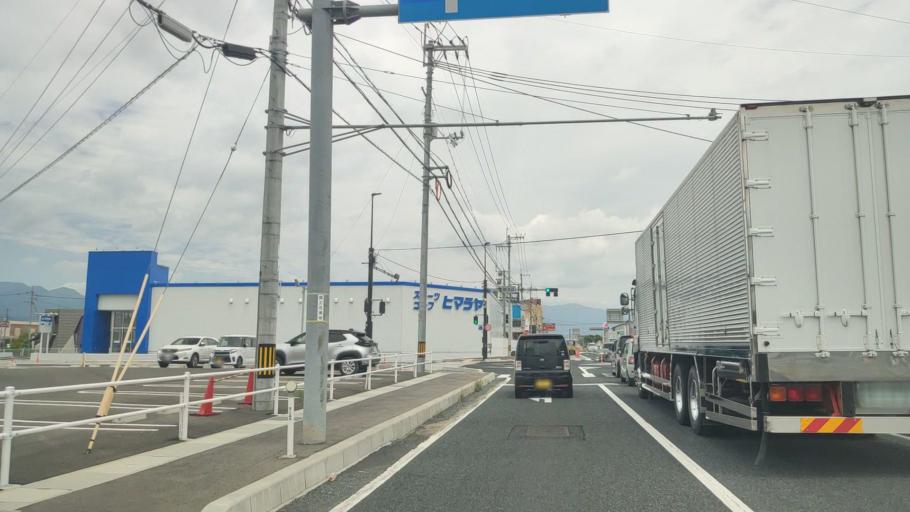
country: JP
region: Okayama
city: Tsuyama
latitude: 35.0608
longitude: 134.0452
